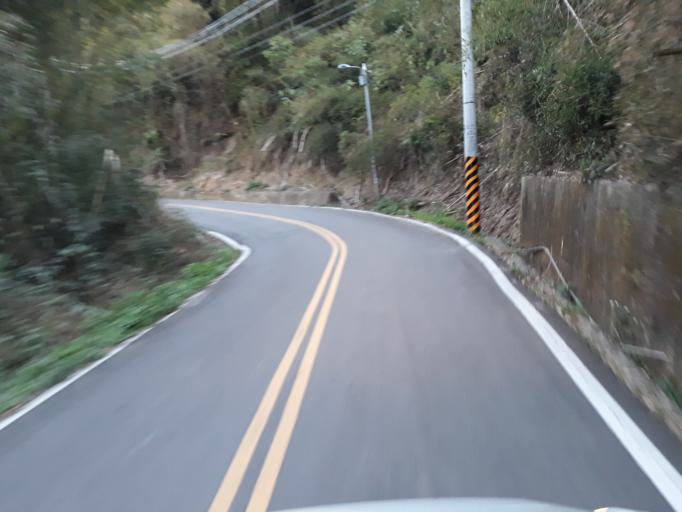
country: TW
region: Taiwan
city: Fengyuan
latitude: 24.3601
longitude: 120.8691
